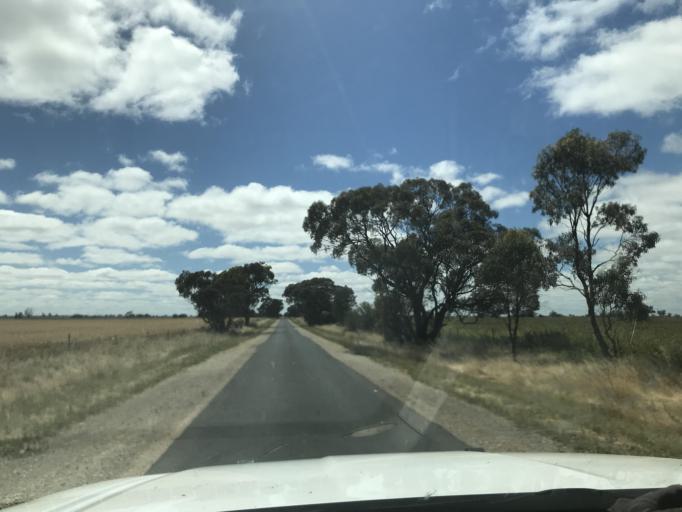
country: AU
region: South Australia
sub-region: Tatiara
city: Bordertown
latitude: -36.2794
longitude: 141.1248
